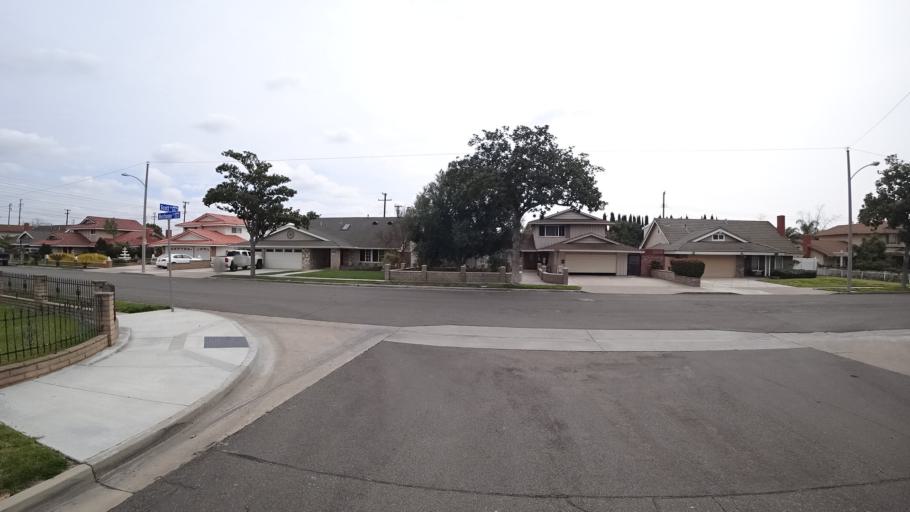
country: US
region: California
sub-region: Orange County
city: Stanton
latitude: 33.8235
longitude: -117.9832
